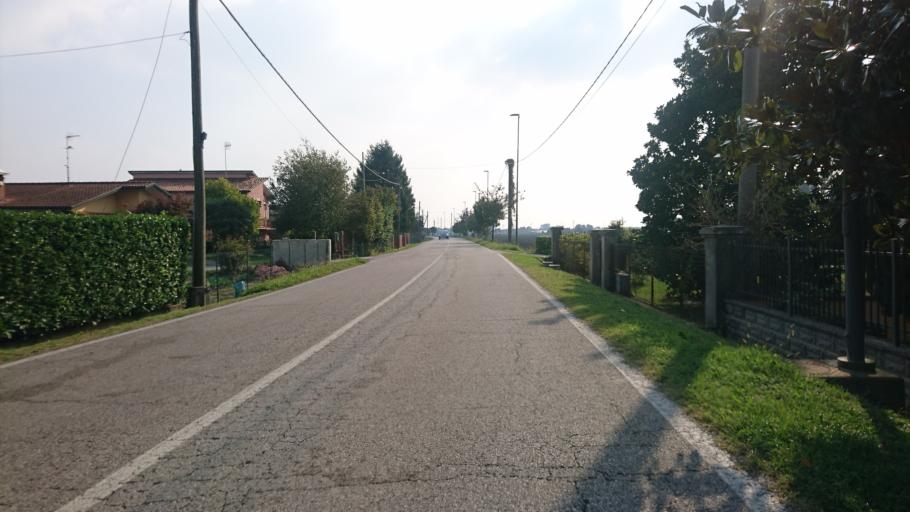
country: IT
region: Veneto
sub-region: Provincia di Rovigo
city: Arqua Polesine
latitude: 45.0215
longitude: 11.7421
